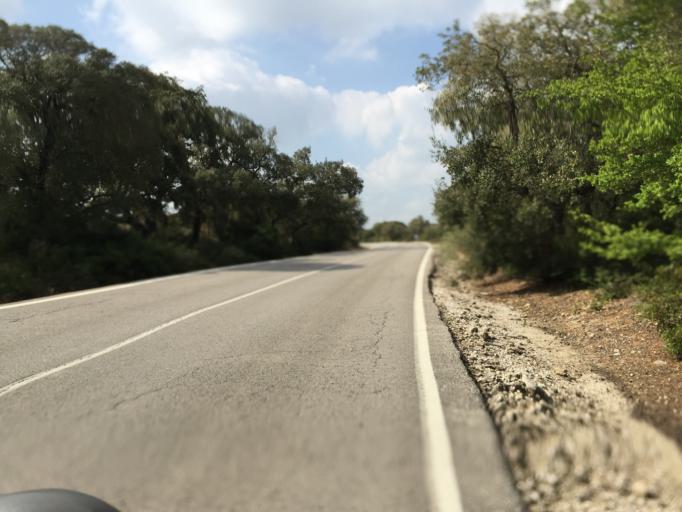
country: ES
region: Andalusia
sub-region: Provincia de Cadiz
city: Vejer de la Frontera
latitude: 36.2998
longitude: -5.9105
